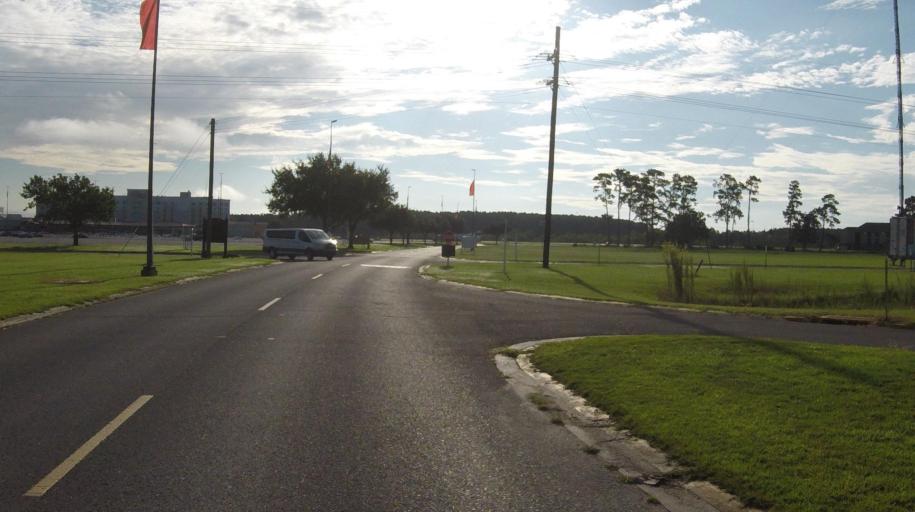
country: US
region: Louisiana
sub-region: Allen Parish
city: Kinder
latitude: 30.5429
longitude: -92.8185
